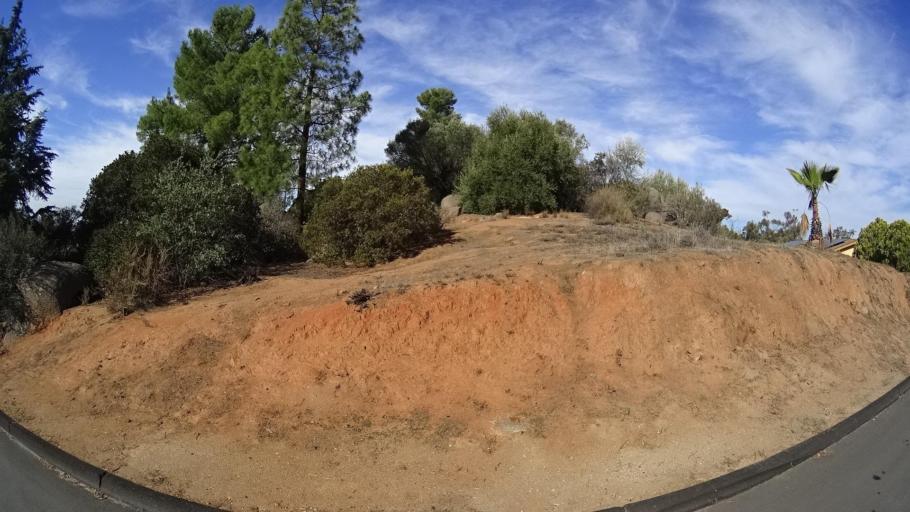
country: US
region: California
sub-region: San Diego County
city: Alpine
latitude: 32.8144
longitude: -116.7741
